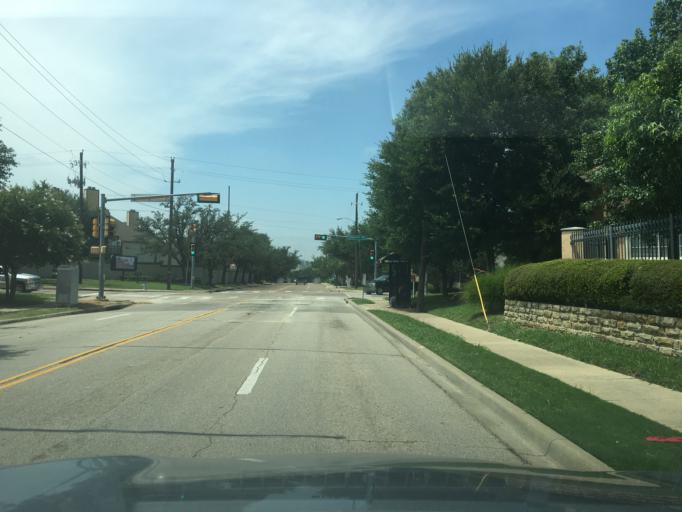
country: US
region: Texas
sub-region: Dallas County
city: Richardson
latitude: 32.9368
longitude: -96.7539
